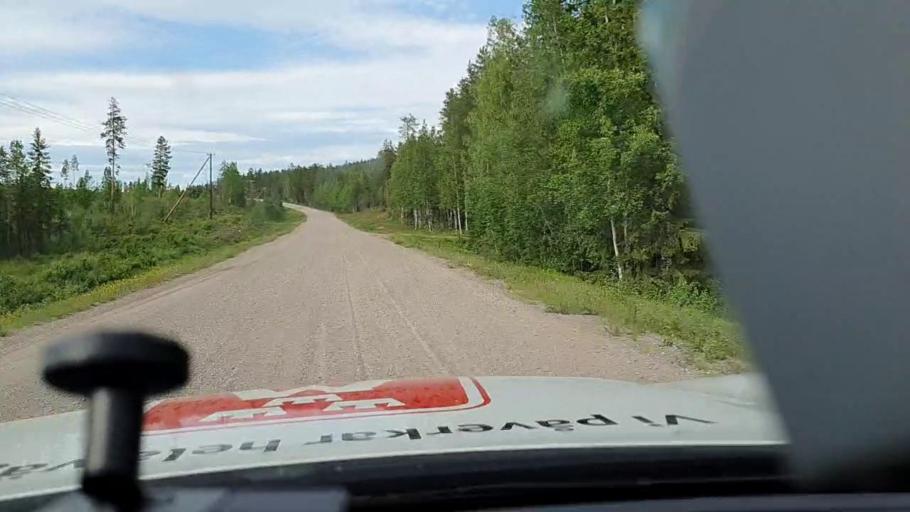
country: SE
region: Norrbotten
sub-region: Alvsbyns Kommun
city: AElvsbyn
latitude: 66.1272
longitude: 20.9972
